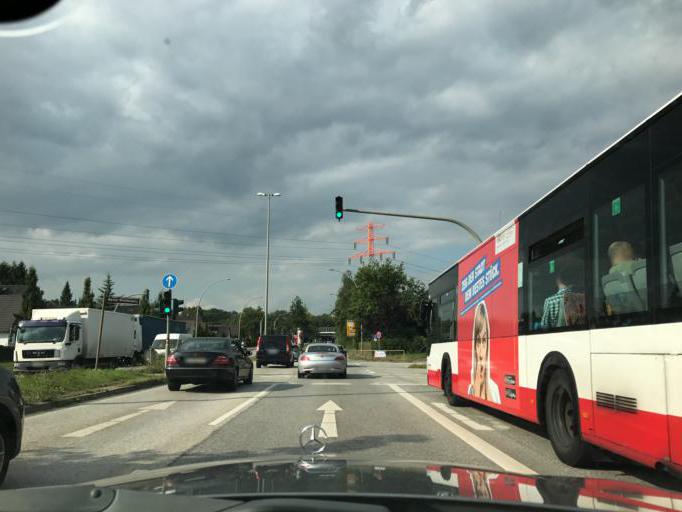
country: DE
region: Hamburg
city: Marienthal
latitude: 53.5419
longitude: 10.0838
